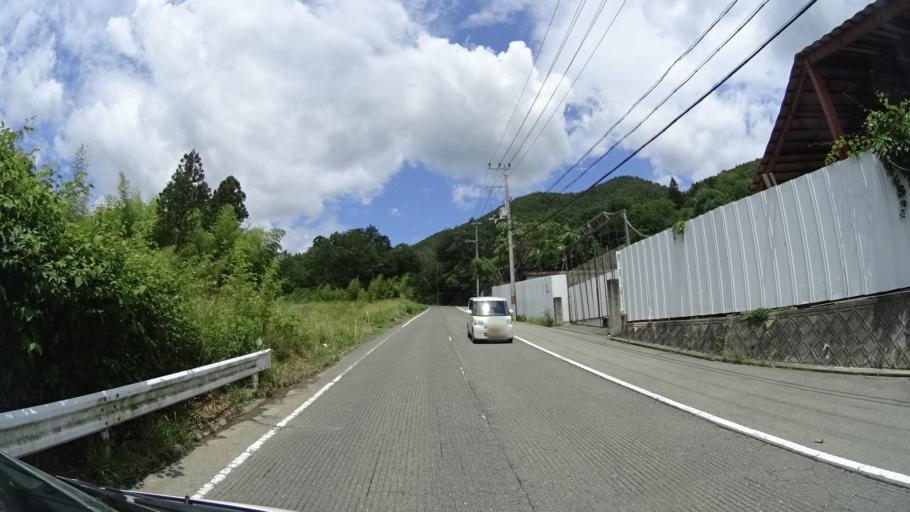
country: JP
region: Kyoto
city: Kameoka
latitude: 35.0073
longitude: 135.4716
